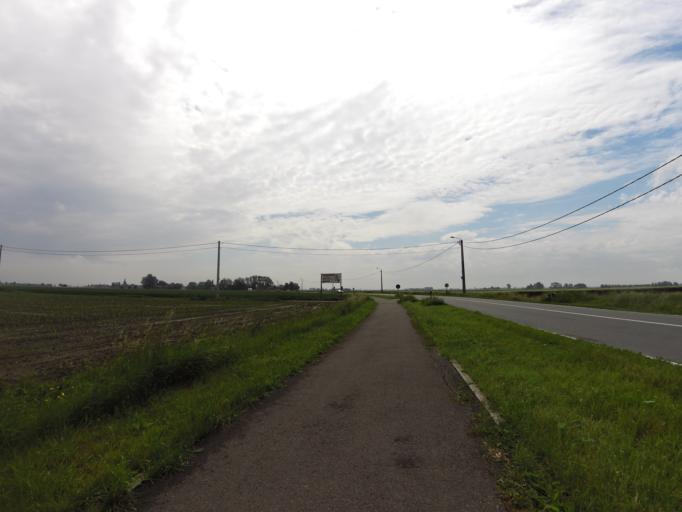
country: BE
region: Flanders
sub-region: Provincie West-Vlaanderen
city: Middelkerke
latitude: 51.1597
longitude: 2.8304
